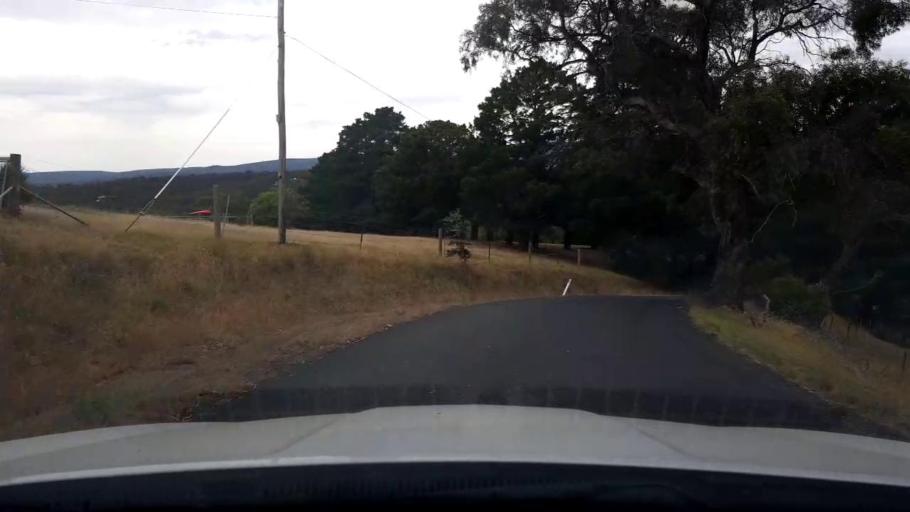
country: AU
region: Victoria
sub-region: Whittlesea
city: Whittlesea
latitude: -37.4899
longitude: 145.0546
